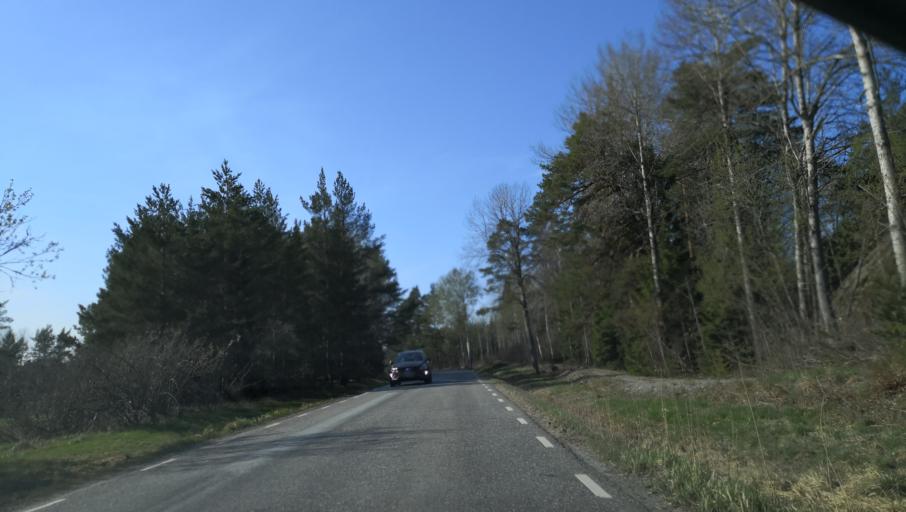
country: SE
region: Stockholm
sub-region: Varmdo Kommun
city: Hemmesta
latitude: 59.3230
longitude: 18.5507
